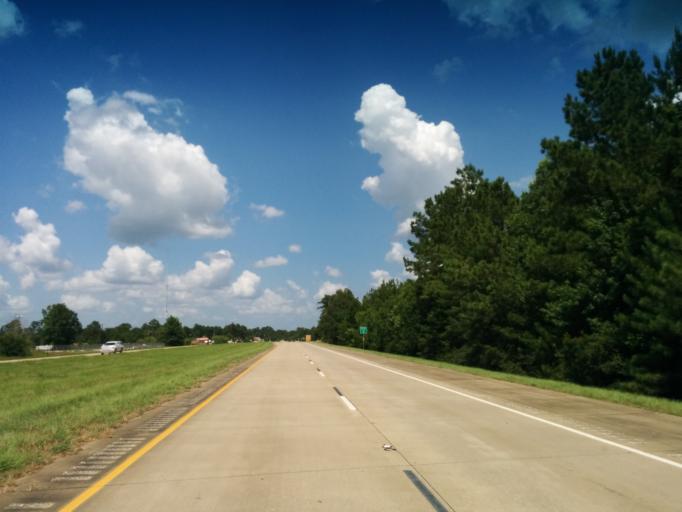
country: US
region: Texas
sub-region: Jasper County
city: Buna
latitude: 30.4241
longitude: -93.9868
